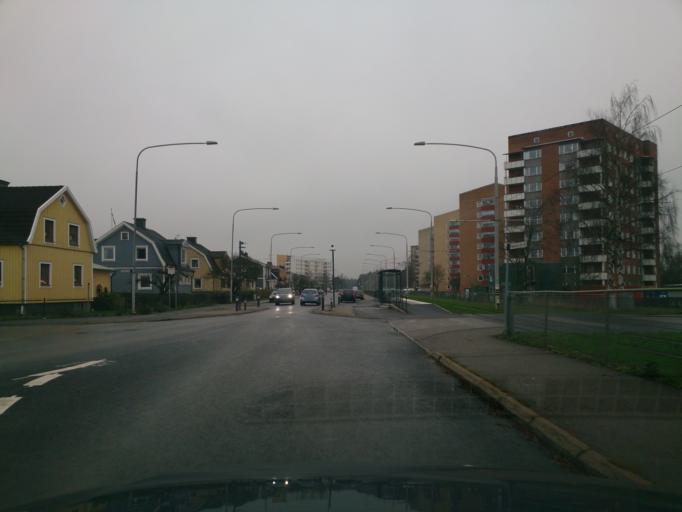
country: SE
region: OEstergoetland
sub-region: Norrkopings Kommun
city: Norrkoping
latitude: 58.6062
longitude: 16.1549
